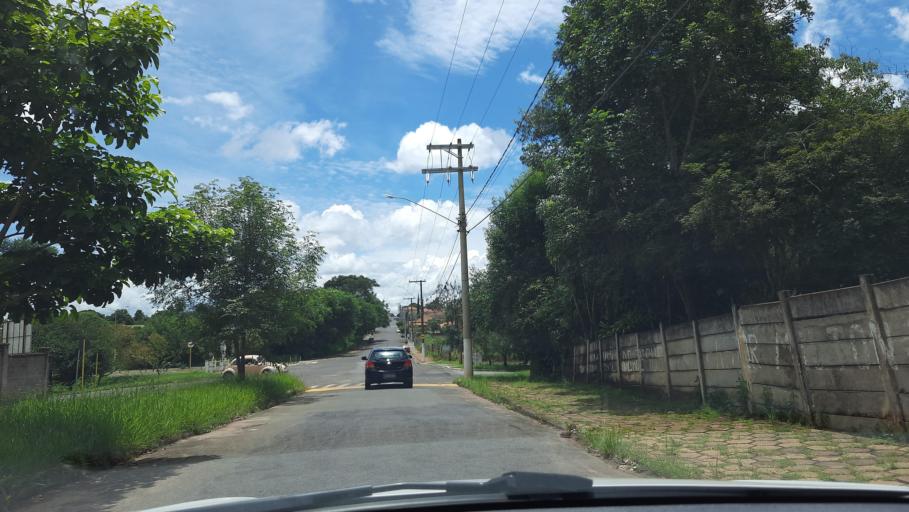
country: BR
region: Sao Paulo
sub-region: Casa Branca
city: Casa Branca
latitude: -21.7815
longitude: -47.0887
